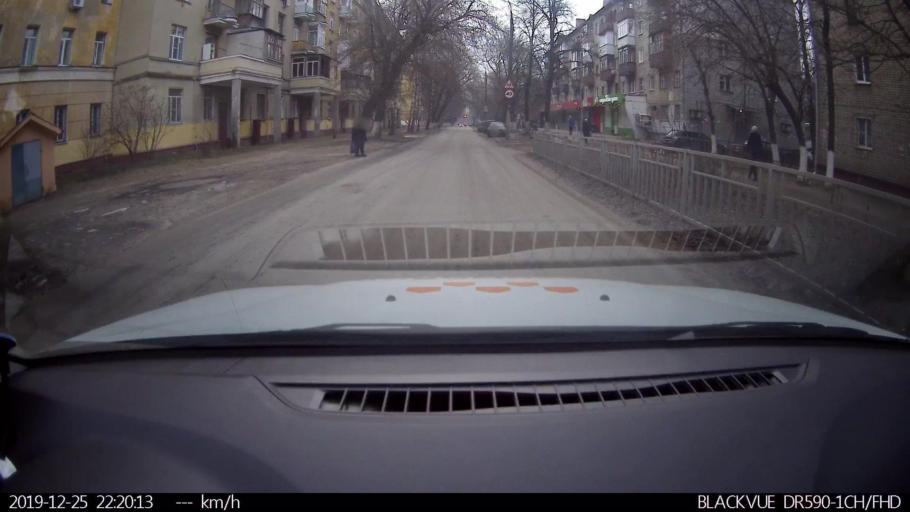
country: RU
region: Nizjnij Novgorod
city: Gorbatovka
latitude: 56.2464
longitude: 43.8469
